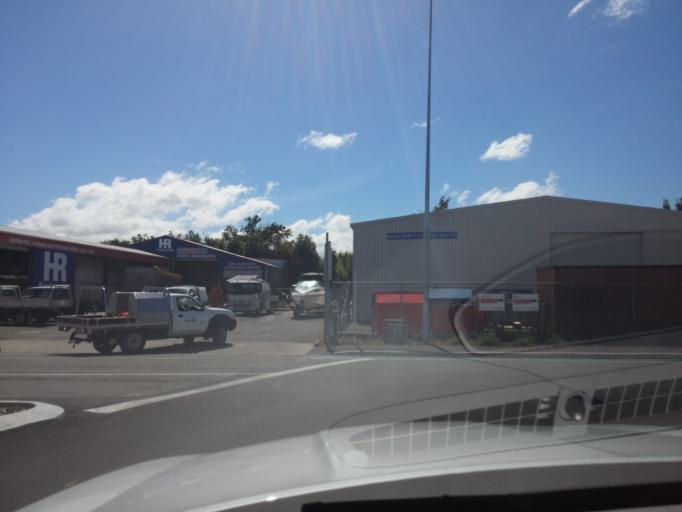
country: NZ
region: Marlborough
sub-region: Marlborough District
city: Blenheim
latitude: -41.5090
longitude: 173.9396
